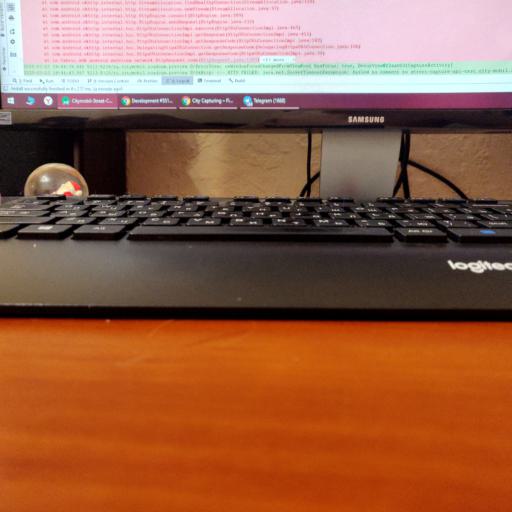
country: FI
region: Haeme
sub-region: Forssa
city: Jokioinen
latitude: 60.8085
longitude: 23.4615
